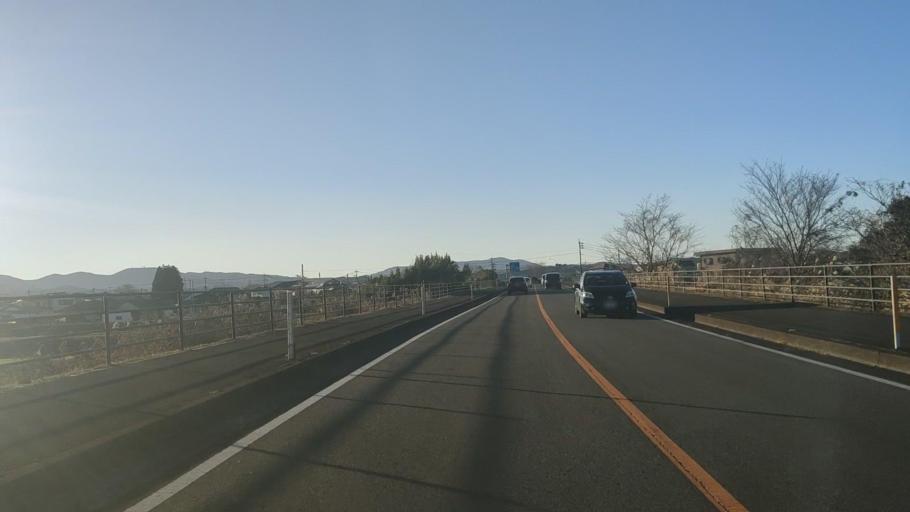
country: JP
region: Miyazaki
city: Miyazaki-shi
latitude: 31.8313
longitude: 131.3032
